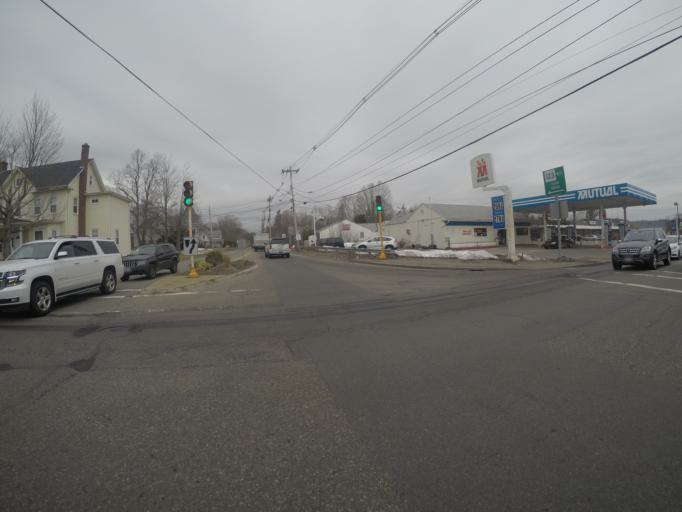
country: US
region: Massachusetts
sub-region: Bristol County
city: Easton
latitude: 42.0424
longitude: -71.0776
